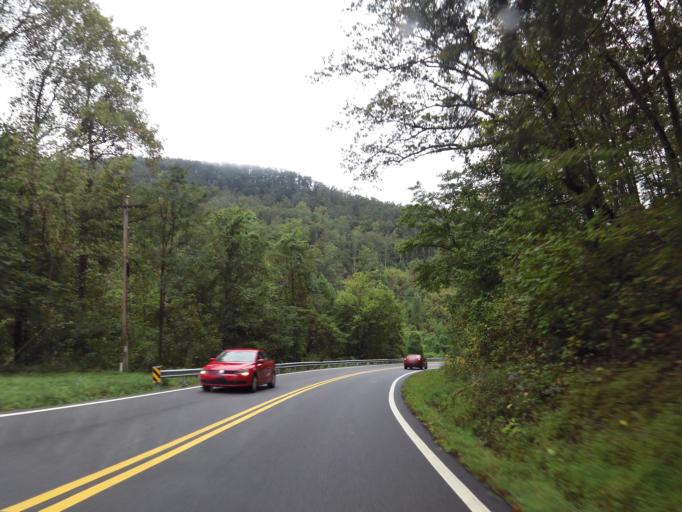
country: US
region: Tennessee
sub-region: Hamilton County
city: Lakesite
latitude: 35.1731
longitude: -85.0074
